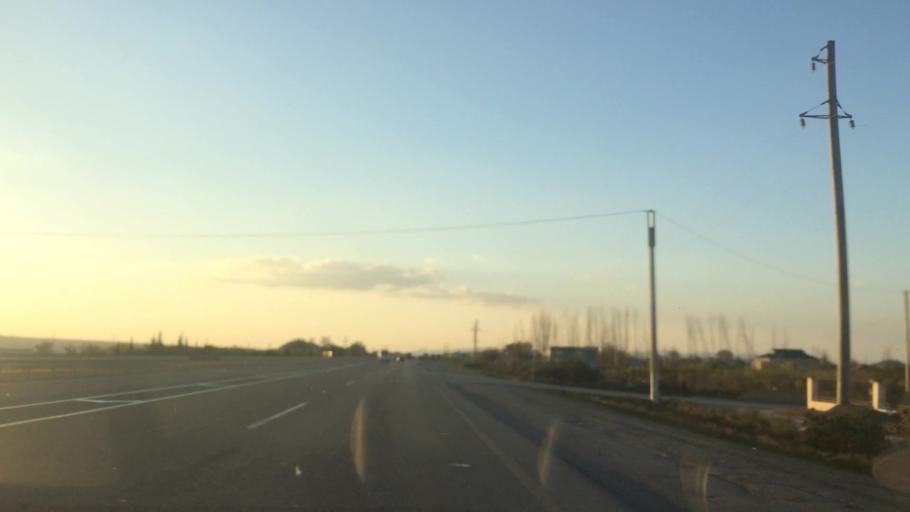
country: AZ
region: Haciqabul
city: Haciqabul
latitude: 40.0077
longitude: 49.1570
